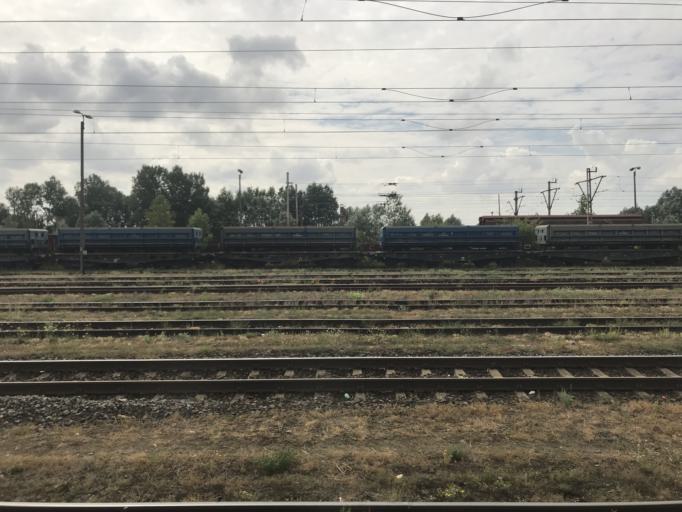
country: PL
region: Greater Poland Voivodeship
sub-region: Powiat gnieznienski
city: Gniezno
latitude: 52.5299
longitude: 17.6095
